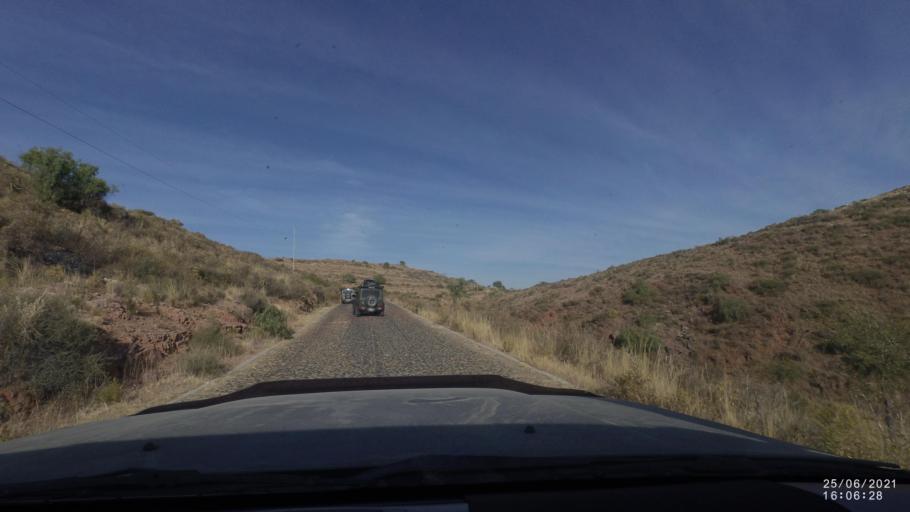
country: BO
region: Cochabamba
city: Cliza
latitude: -17.6668
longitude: -65.9071
